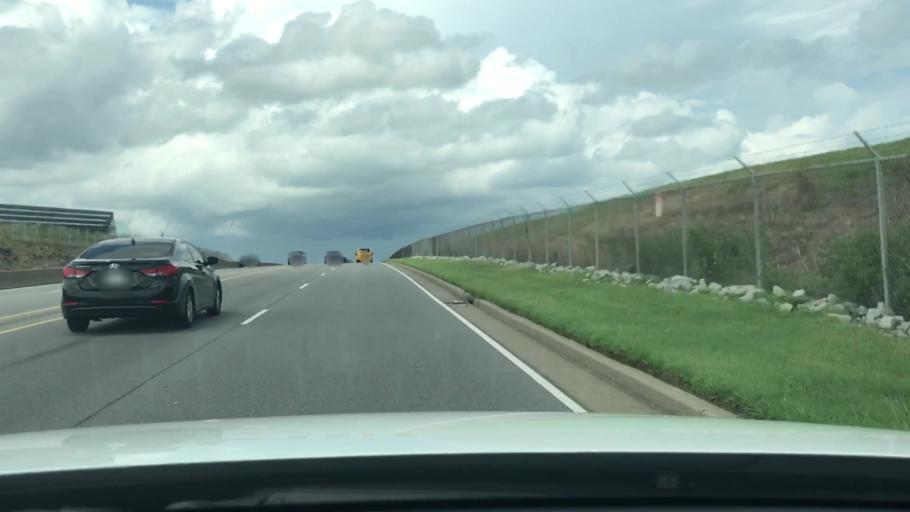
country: US
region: Tennessee
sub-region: Davidson County
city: Oak Hill
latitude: 36.1187
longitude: -86.6673
